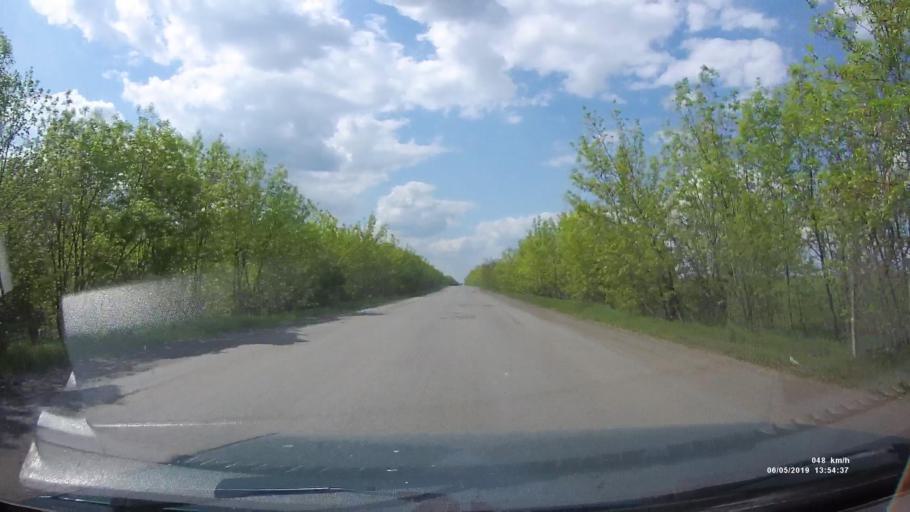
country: RU
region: Rostov
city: Melikhovskaya
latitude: 47.6745
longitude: 40.4474
